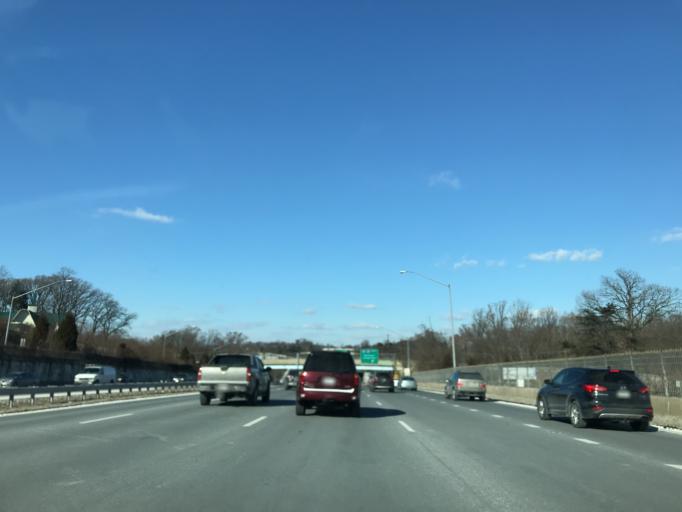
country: US
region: Maryland
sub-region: Prince George's County
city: Camp Springs
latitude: 38.8147
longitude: -76.9137
